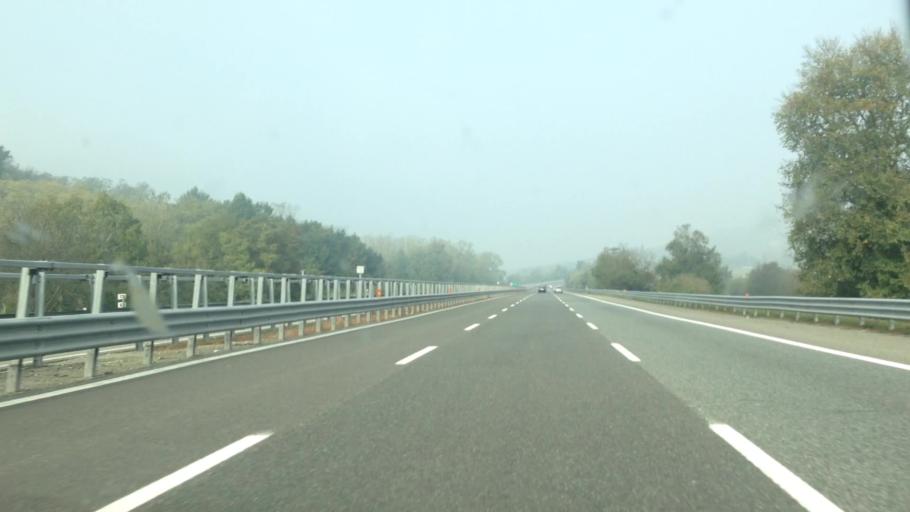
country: IT
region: Piedmont
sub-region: Provincia di Alessandria
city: Castelletto Monferrato
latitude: 44.9775
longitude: 8.5463
